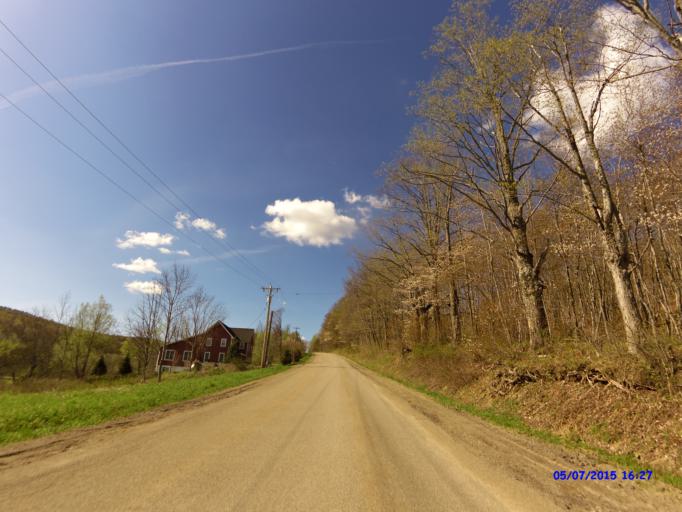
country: US
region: New York
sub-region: Cattaraugus County
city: Little Valley
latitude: 42.3015
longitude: -78.6789
